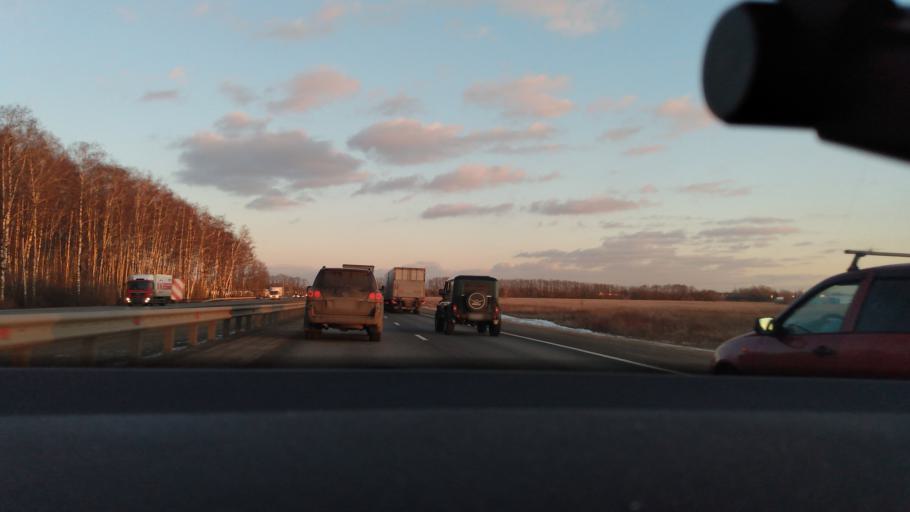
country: RU
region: Moskovskaya
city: Raduzhnyy
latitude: 55.1494
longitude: 38.7147
